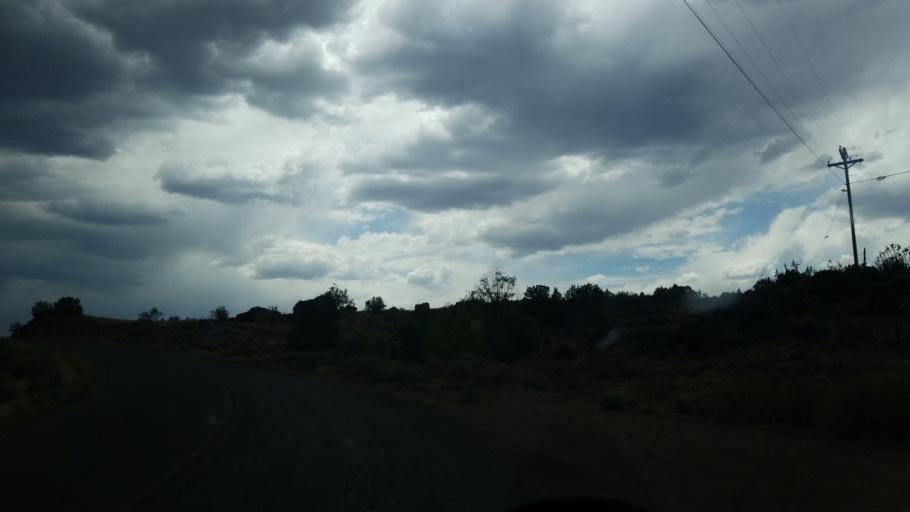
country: US
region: New Mexico
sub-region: Cibola County
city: Grants
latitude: 35.1611
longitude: -107.8488
